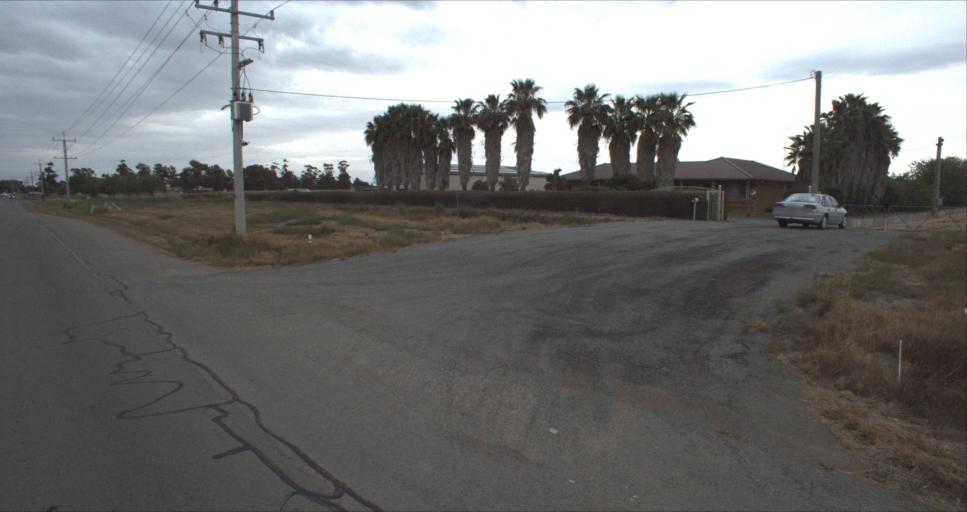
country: AU
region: New South Wales
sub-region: Leeton
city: Leeton
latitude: -34.5461
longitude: 146.3860
